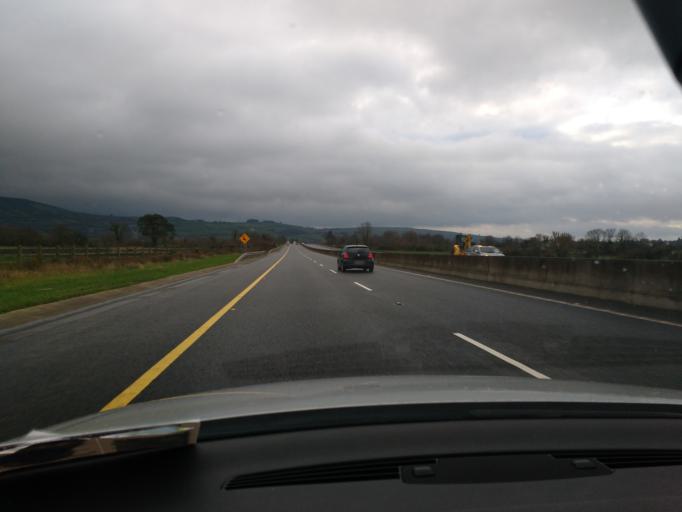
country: IE
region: Munster
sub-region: North Tipperary
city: Nenagh
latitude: 52.8122
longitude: -8.3106
